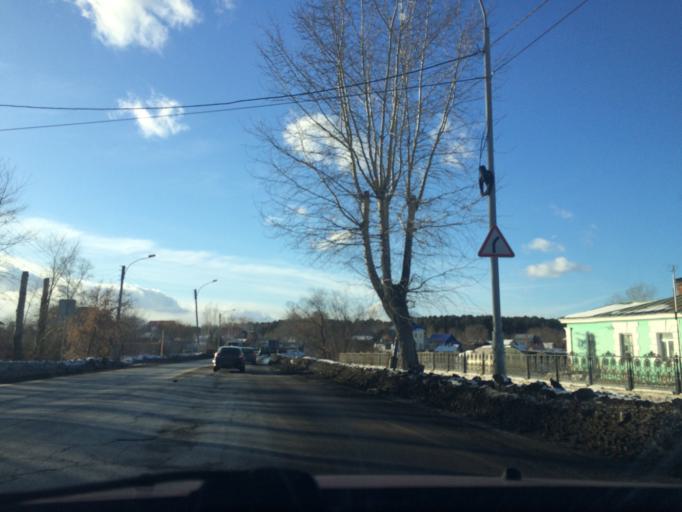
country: RU
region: Sverdlovsk
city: Istok
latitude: 56.7735
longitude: 60.8105
